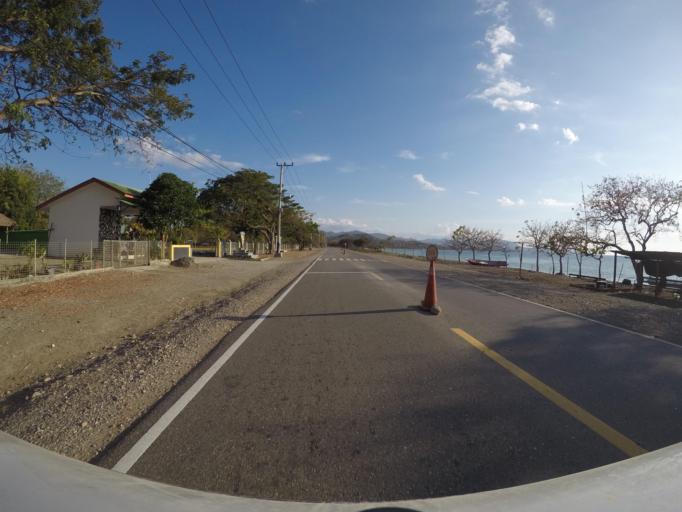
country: ID
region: East Nusa Tenggara
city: Atambua
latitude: -8.9326
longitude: 124.9807
